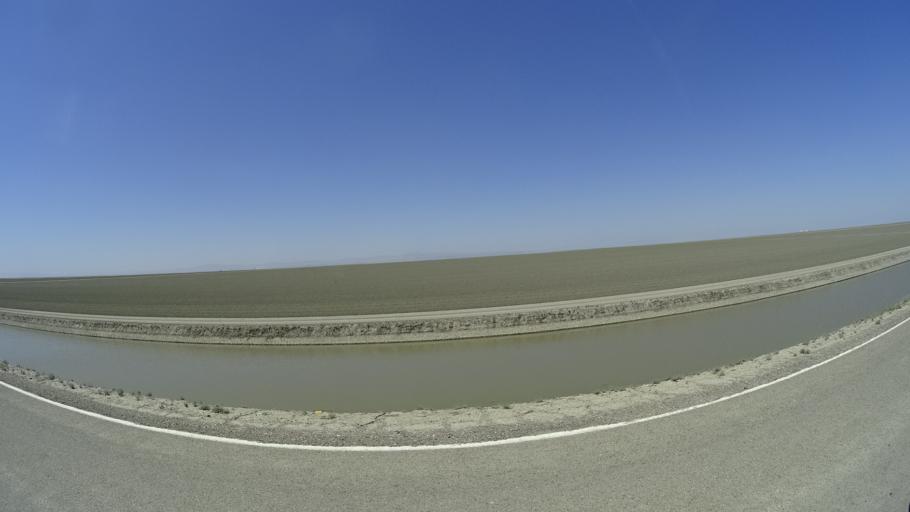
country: US
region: California
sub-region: Kings County
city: Corcoran
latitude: 35.9732
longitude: -119.6432
